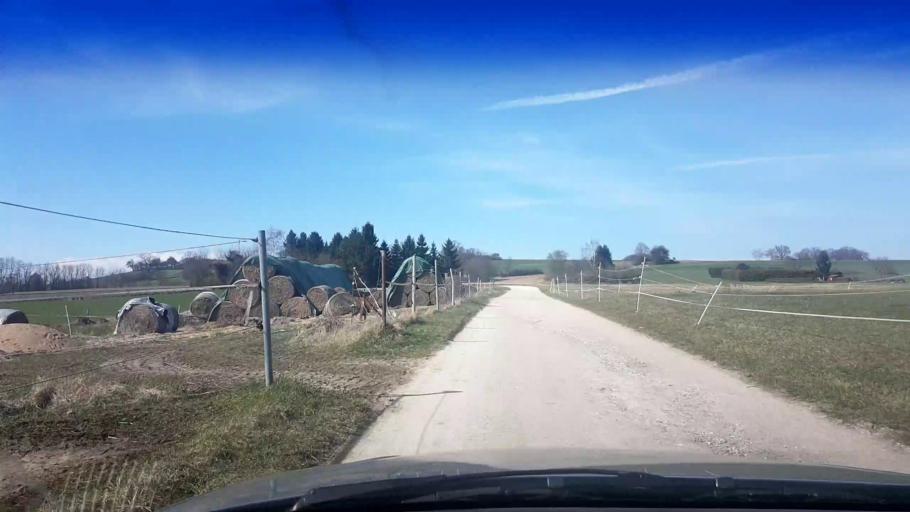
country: DE
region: Bavaria
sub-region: Upper Franconia
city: Bischberg
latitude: 49.8951
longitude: 10.8281
